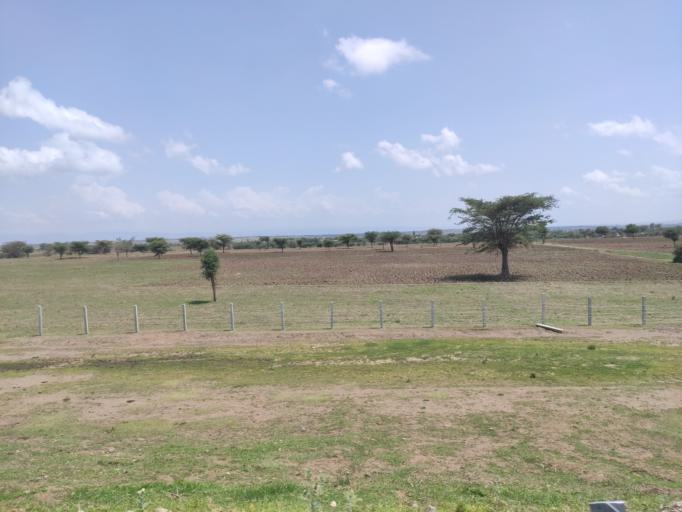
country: ET
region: Oromiya
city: Ziway
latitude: 8.2681
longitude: 38.9058
